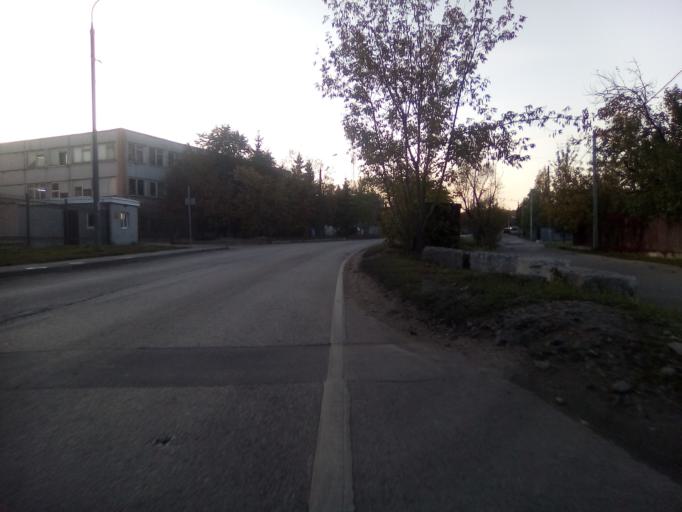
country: RU
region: Moskovskaya
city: Kokoshkino
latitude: 55.6056
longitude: 37.1888
